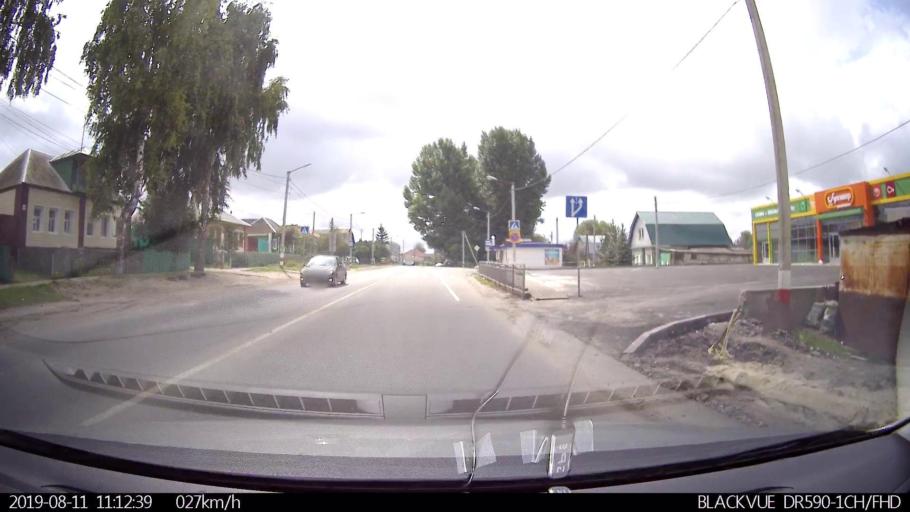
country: RU
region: Ulyanovsk
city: Novoul'yanovsk
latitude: 54.2223
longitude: 48.2975
